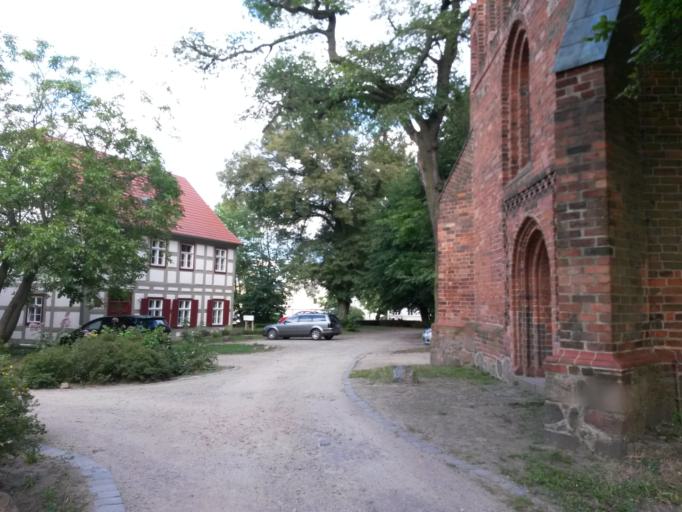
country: DE
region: Brandenburg
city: Angermunde
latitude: 53.0194
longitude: 14.0025
